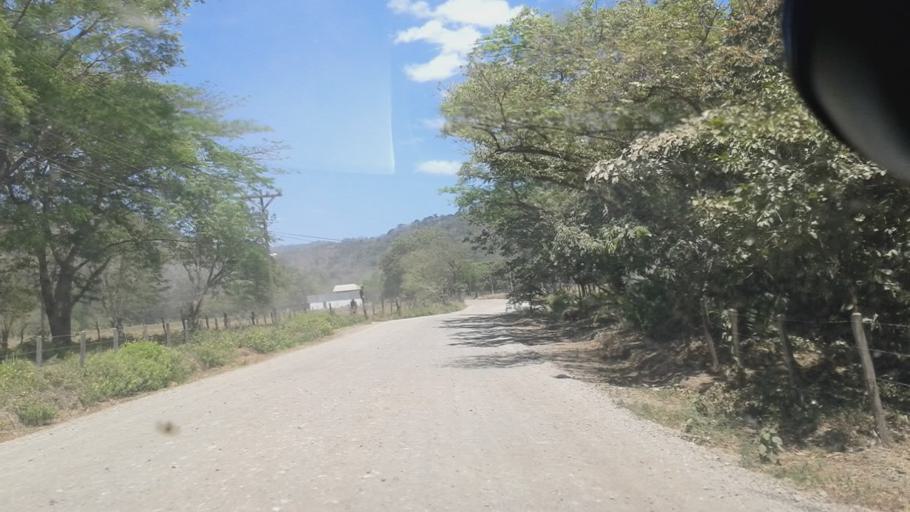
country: CR
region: Guanacaste
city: Samara
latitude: 9.9934
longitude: -85.6792
